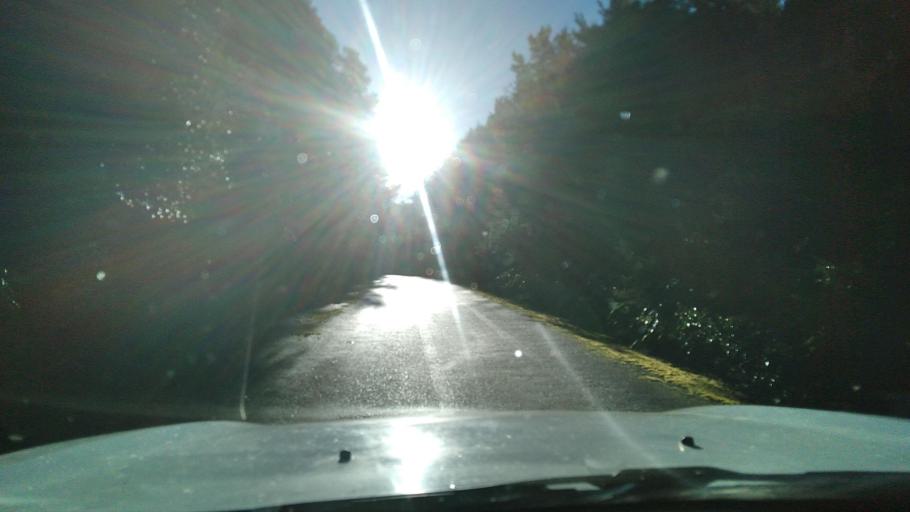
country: NZ
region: Waikato
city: Turangi
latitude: -39.1741
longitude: 175.8081
